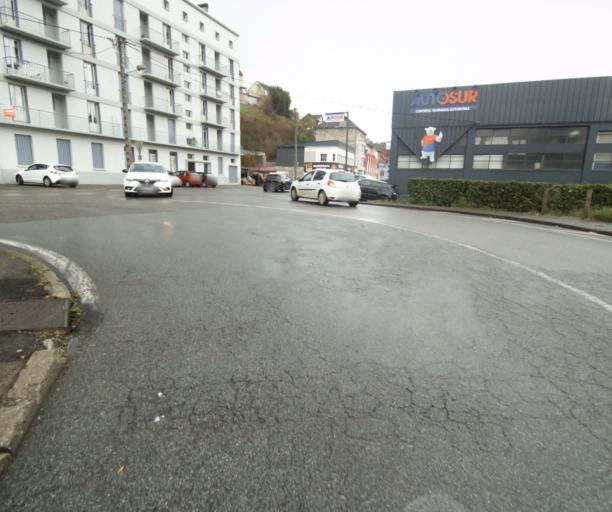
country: FR
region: Limousin
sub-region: Departement de la Correze
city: Tulle
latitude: 45.2560
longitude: 1.7565
